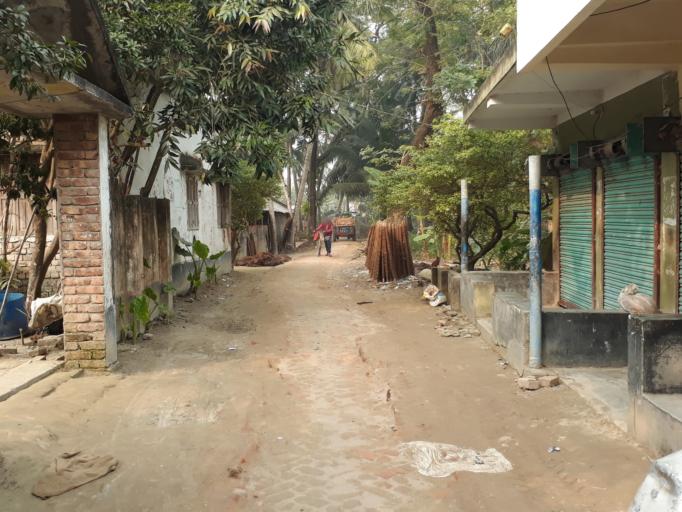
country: BD
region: Khulna
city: Kesabpur
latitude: 22.7885
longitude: 89.2733
